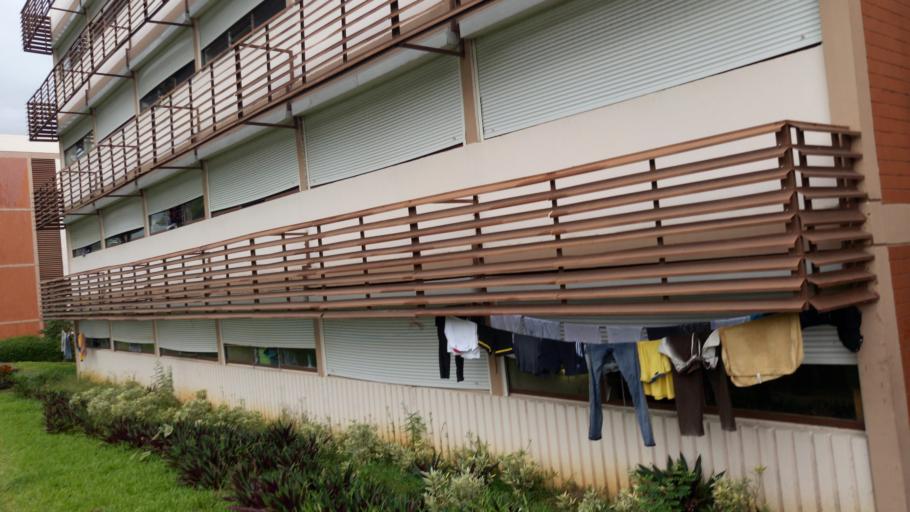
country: CI
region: Lagunes
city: Abidjan
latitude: 5.3387
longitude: -3.9904
